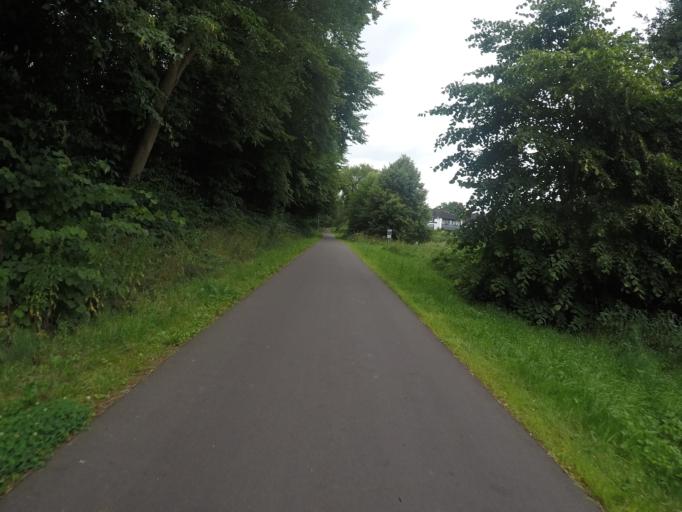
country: DE
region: Lower Saxony
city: Stade
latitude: 53.5983
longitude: 9.4569
